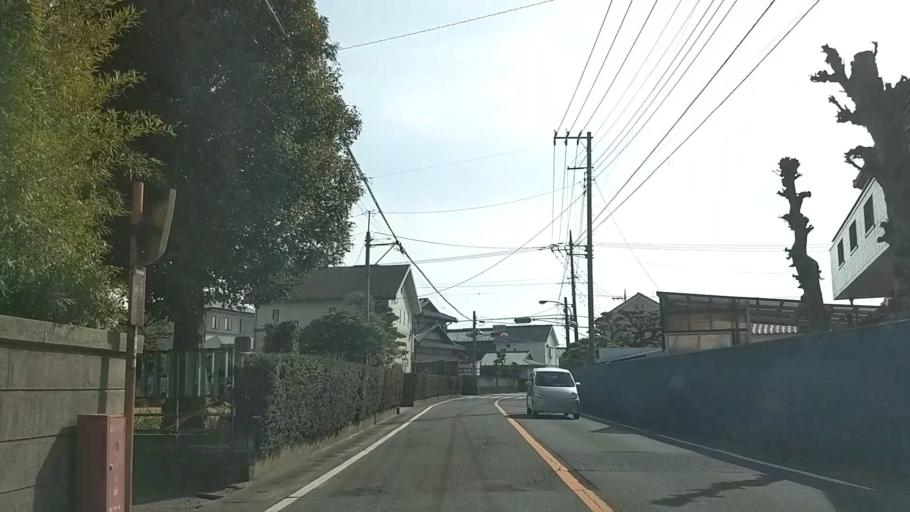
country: JP
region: Kanagawa
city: Chigasaki
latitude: 35.3555
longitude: 139.3847
